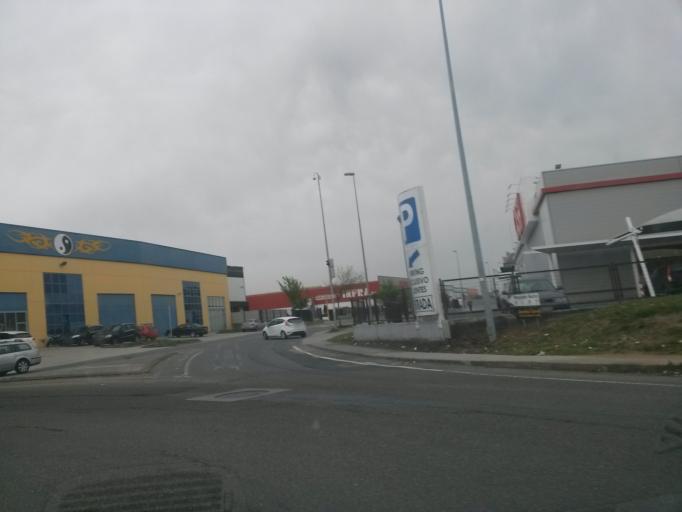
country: ES
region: Galicia
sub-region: Provincia de Lugo
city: Lugo
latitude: 43.0479
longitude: -7.5679
